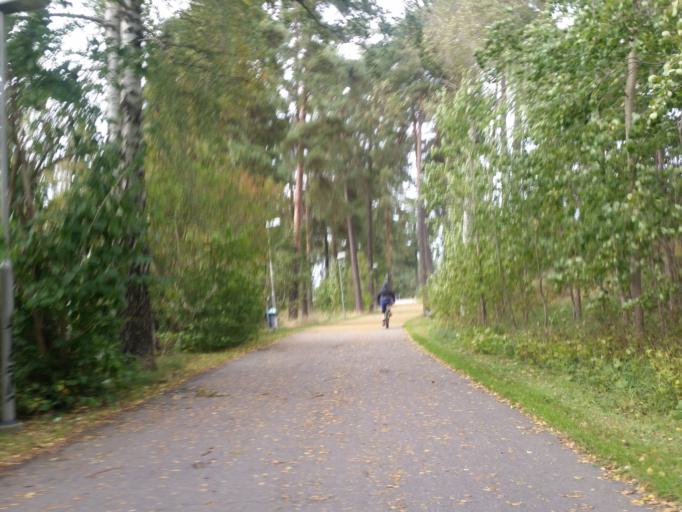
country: SE
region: Stockholm
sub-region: Stockholms Kommun
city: Arsta
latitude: 59.2708
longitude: 18.0941
